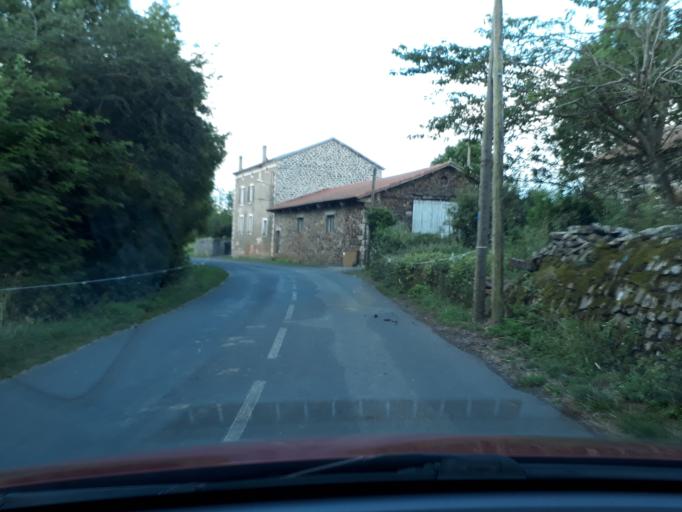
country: FR
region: Languedoc-Roussillon
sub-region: Departement de la Lozere
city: Langogne
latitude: 44.8193
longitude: 3.9307
